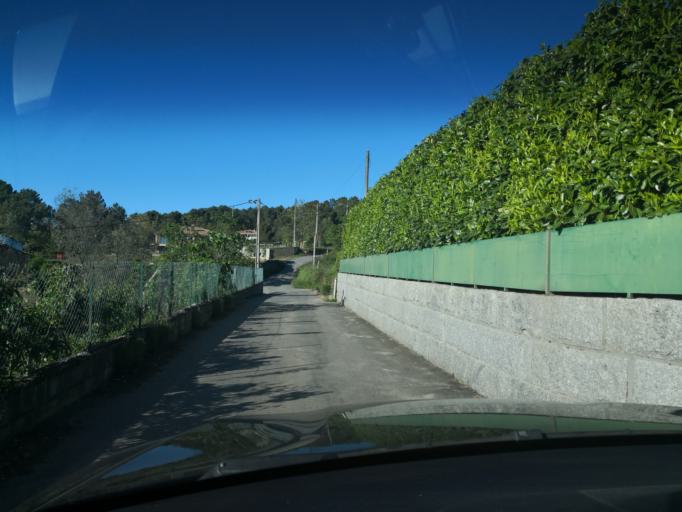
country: PT
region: Vila Real
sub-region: Vila Real
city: Vila Real
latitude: 41.3130
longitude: -7.7020
